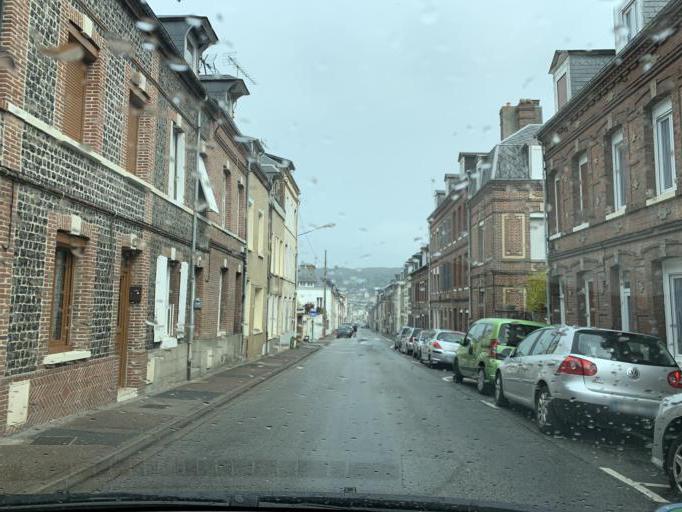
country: FR
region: Haute-Normandie
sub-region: Departement de la Seine-Maritime
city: Fecamp
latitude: 49.7574
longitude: 0.3632
